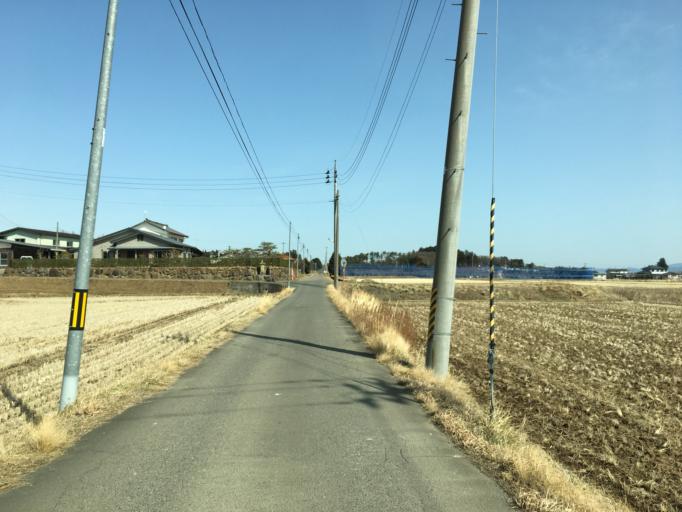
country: JP
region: Fukushima
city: Motomiya
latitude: 37.5424
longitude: 140.3670
